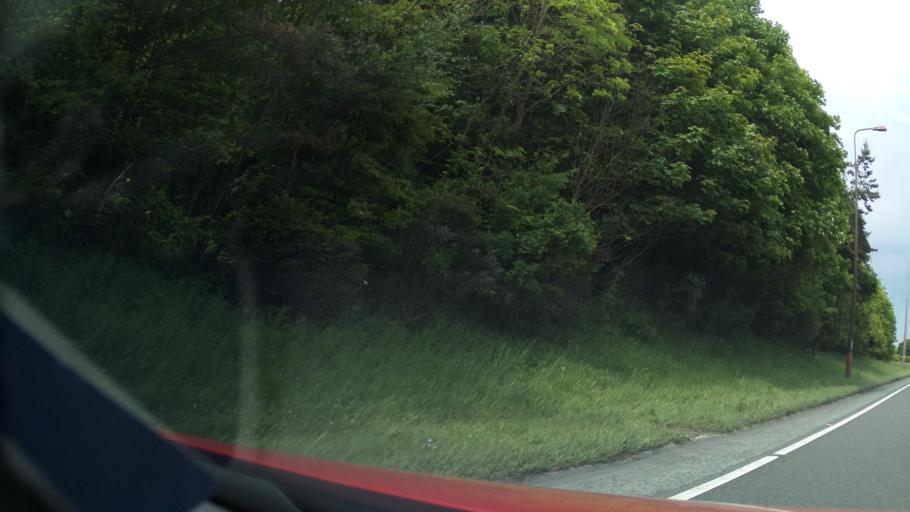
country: GB
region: England
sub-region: County Durham
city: Wingate
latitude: 54.7466
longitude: -1.3641
